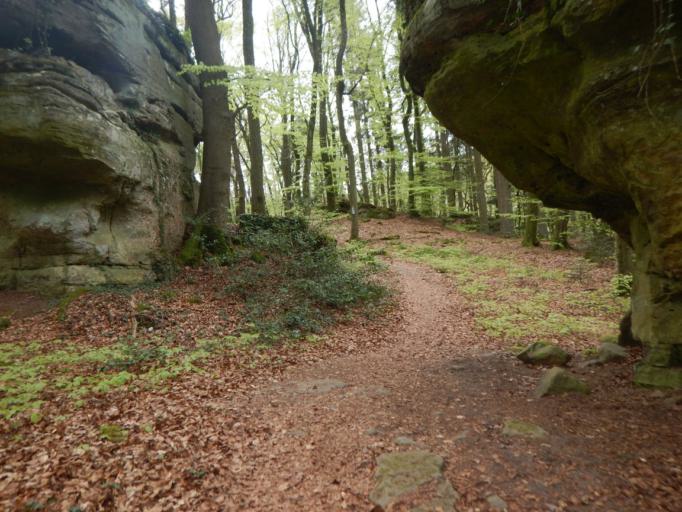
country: LU
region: Grevenmacher
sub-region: Canton d'Echternach
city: Consdorf
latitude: 49.7917
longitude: 6.3191
